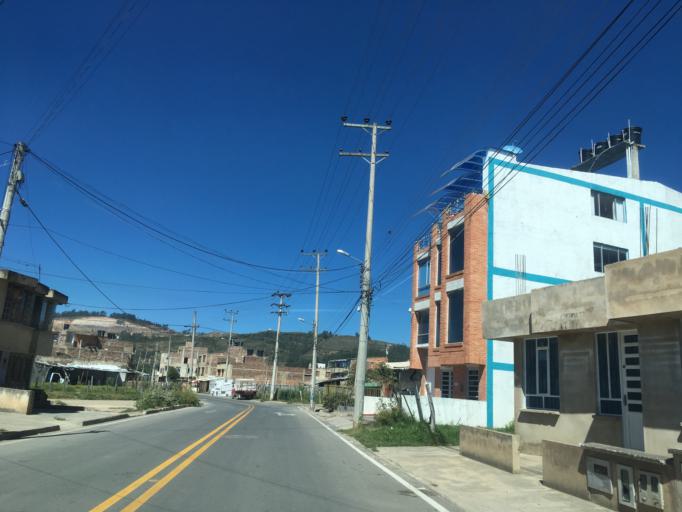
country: CO
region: Boyaca
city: Sogamoso
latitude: 5.7110
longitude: -72.9450
